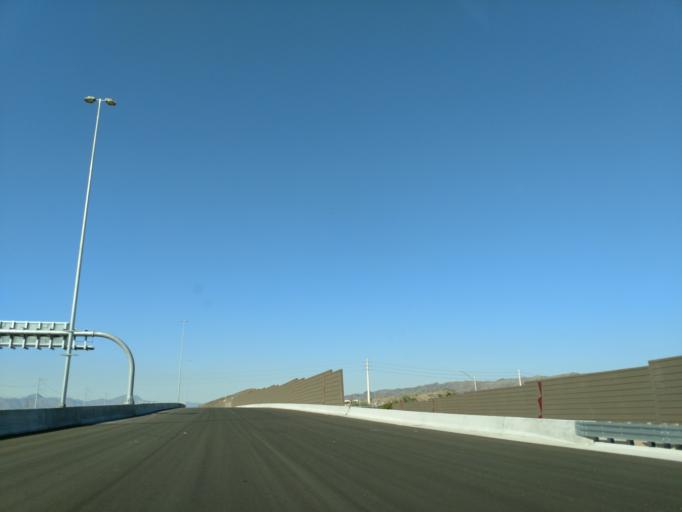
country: US
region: Arizona
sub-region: Maricopa County
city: Guadalupe
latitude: 33.2921
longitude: -112.0286
